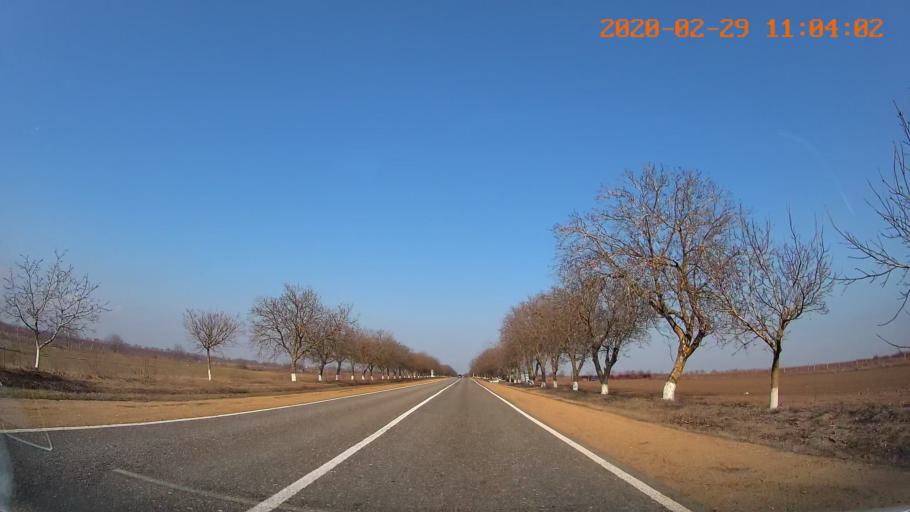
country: MD
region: Criuleni
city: Criuleni
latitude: 47.1839
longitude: 29.2071
